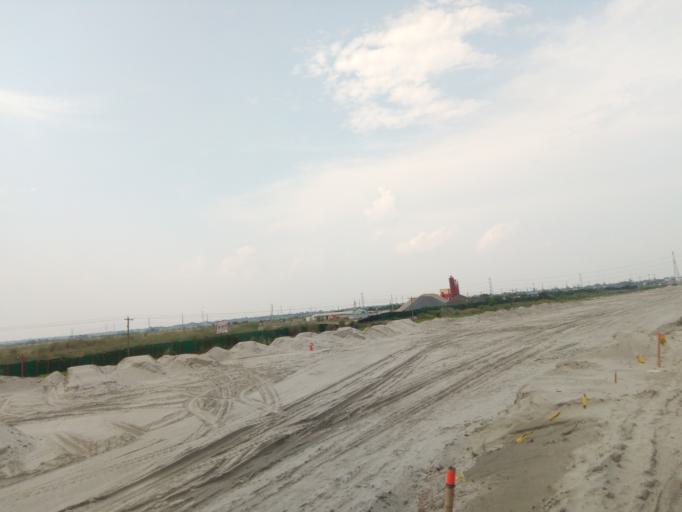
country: BD
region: Dhaka
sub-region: Dhaka
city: Dhaka
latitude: 23.6193
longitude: 90.3356
